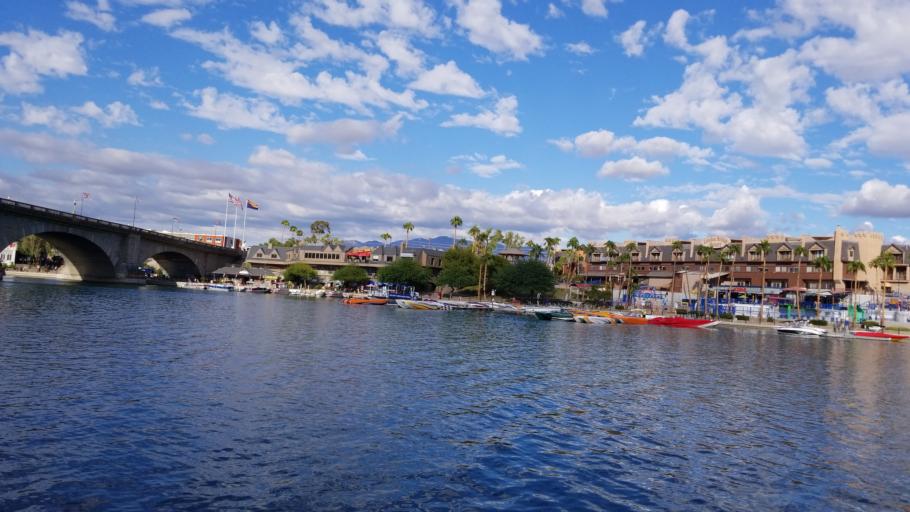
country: US
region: Arizona
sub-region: Mohave County
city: Lake Havasu City
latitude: 34.4703
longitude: -114.3475
